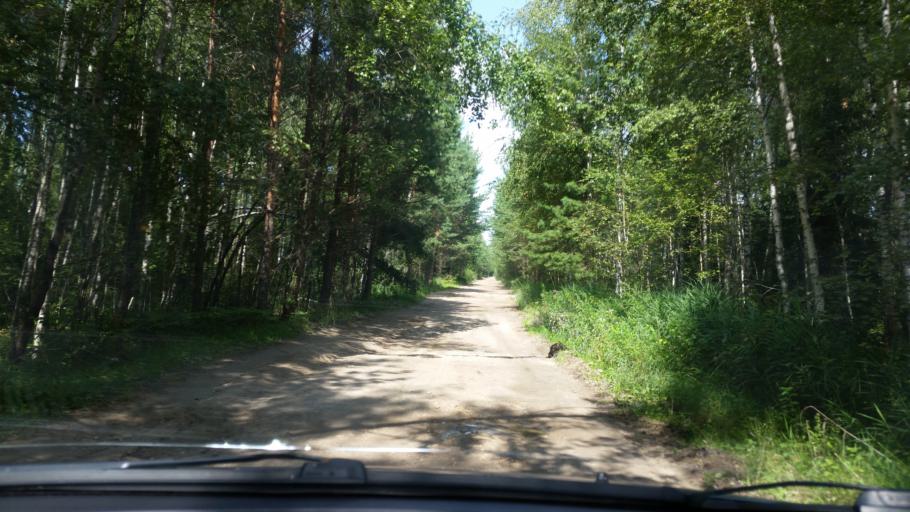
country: RU
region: Moskovskaya
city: Pushchino
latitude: 54.9166
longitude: 37.6855
